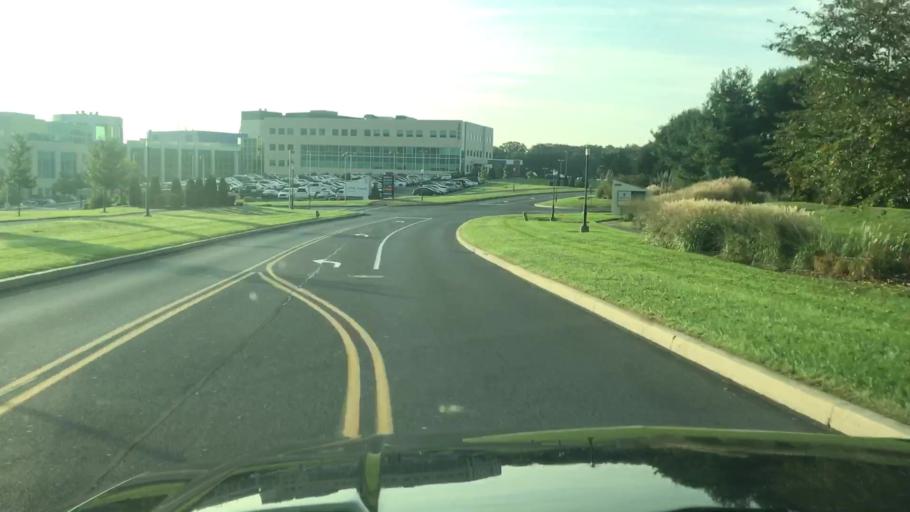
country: US
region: Pennsylvania
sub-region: Cumberland County
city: Enola
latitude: 40.2858
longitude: -76.9772
